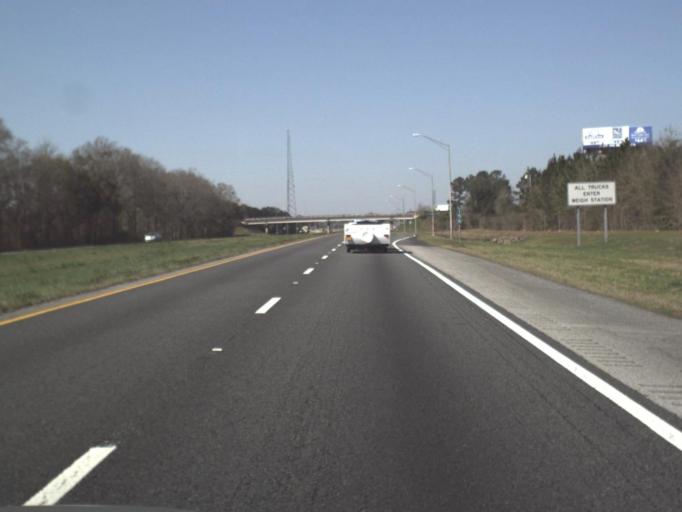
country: US
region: Florida
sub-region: Jackson County
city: Sneads
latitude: 30.6409
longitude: -84.9698
